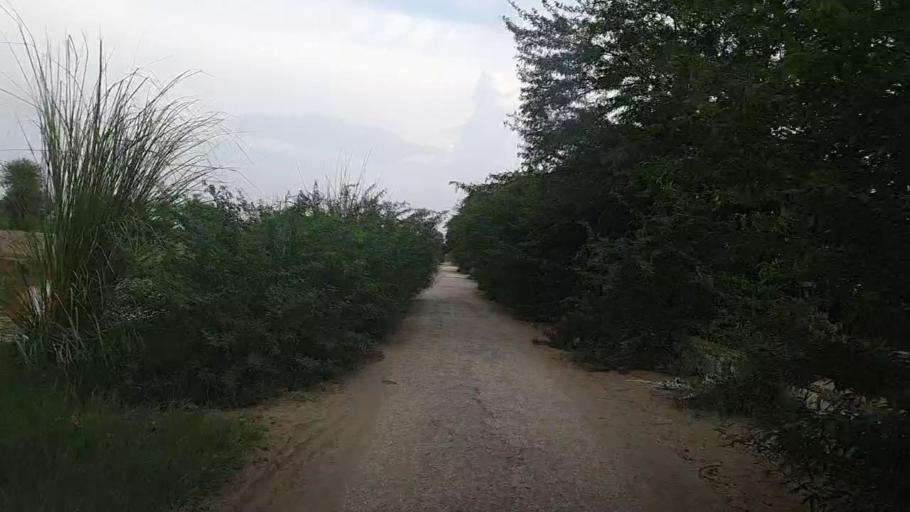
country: PK
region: Sindh
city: Khanpur
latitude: 27.8404
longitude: 69.4156
